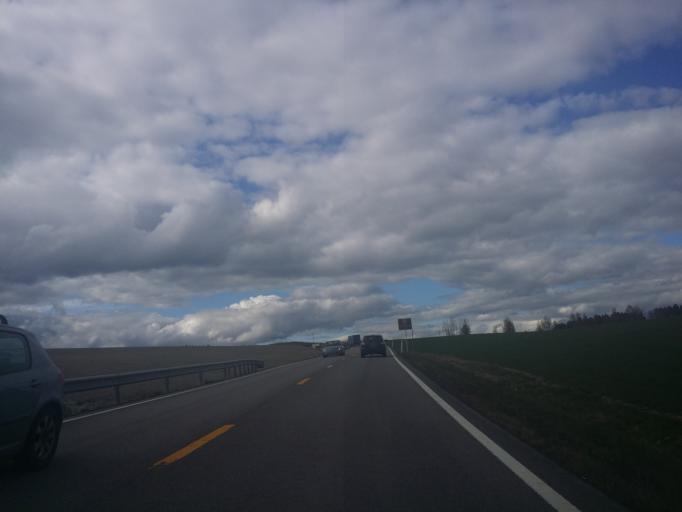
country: NO
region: Buskerud
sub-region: Ringerike
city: Honefoss
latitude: 60.1636
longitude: 10.2194
